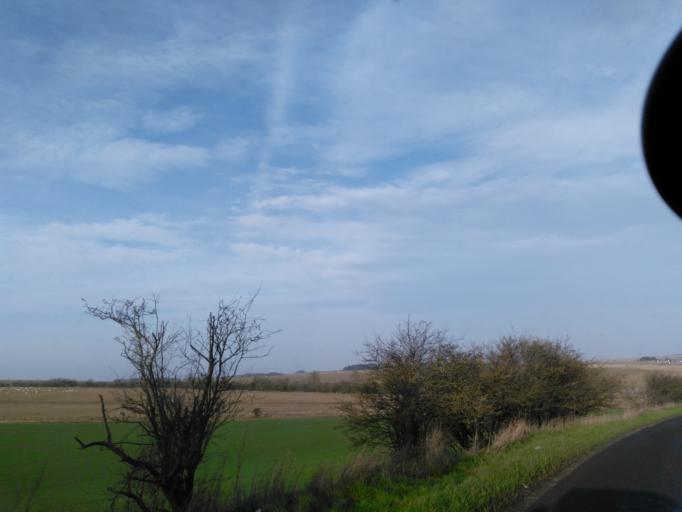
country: GB
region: England
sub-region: Wiltshire
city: Market Lavington
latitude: 51.2317
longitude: -1.9648
